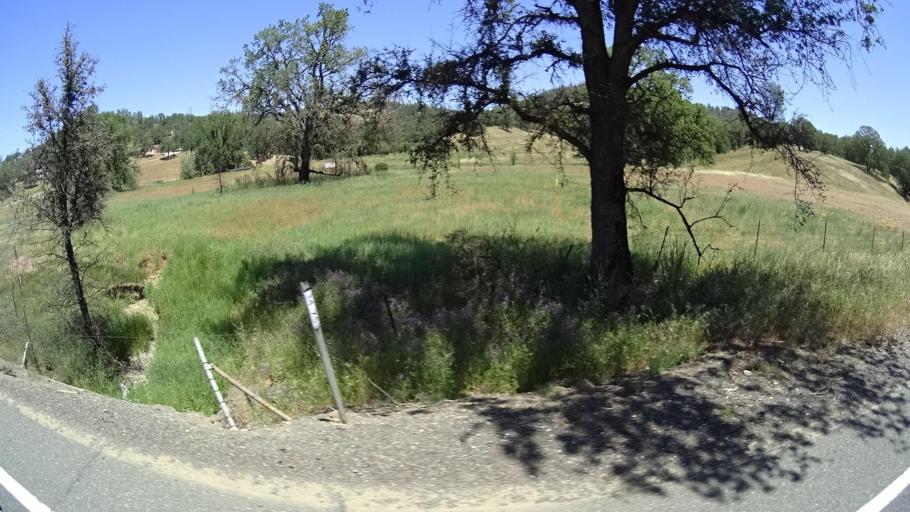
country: US
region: California
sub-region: Lake County
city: Lower Lake
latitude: 38.8464
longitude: -122.6096
